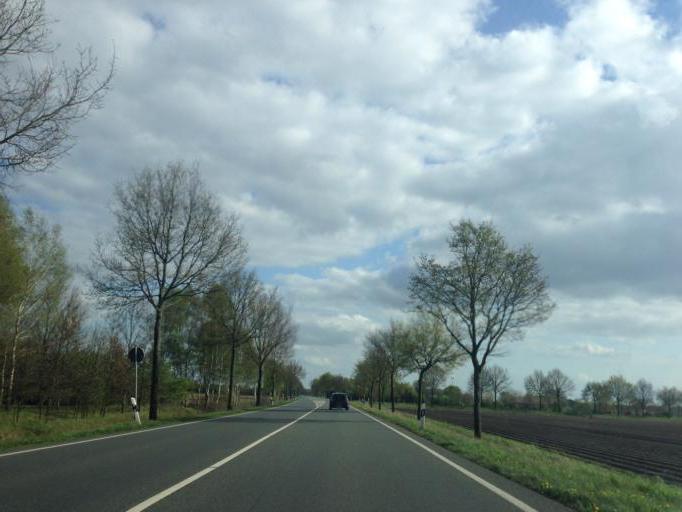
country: DE
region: Lower Saxony
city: Broeckel
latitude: 52.5108
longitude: 10.2261
